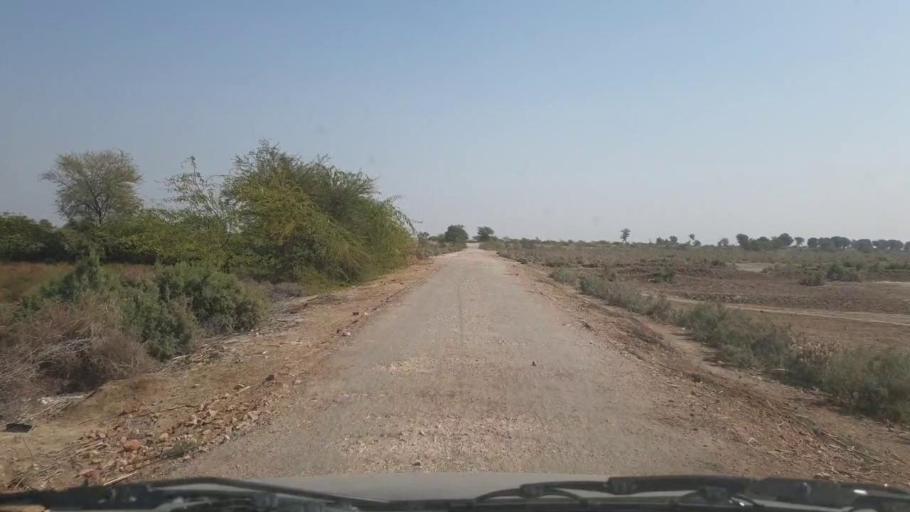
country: PK
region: Sindh
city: Samaro
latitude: 25.2413
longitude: 69.3722
